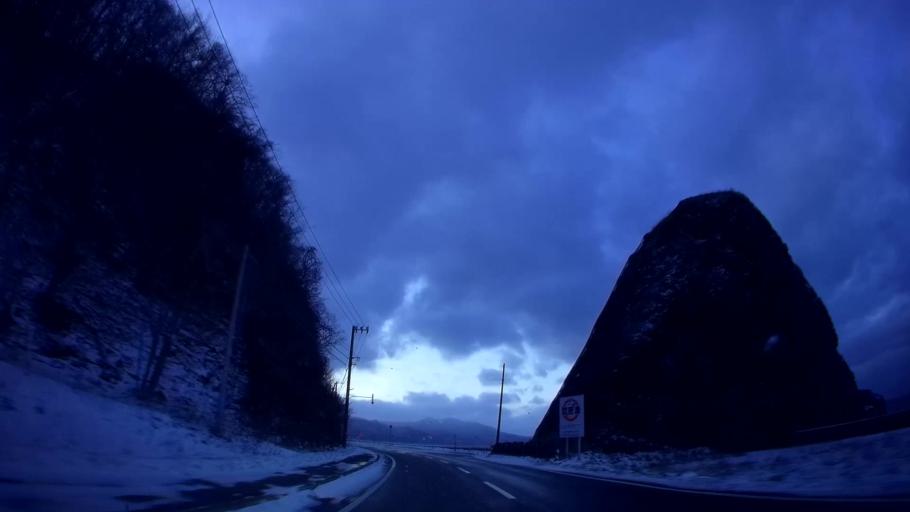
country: JP
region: Hokkaido
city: Hakodate
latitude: 41.8931
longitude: 141.0463
